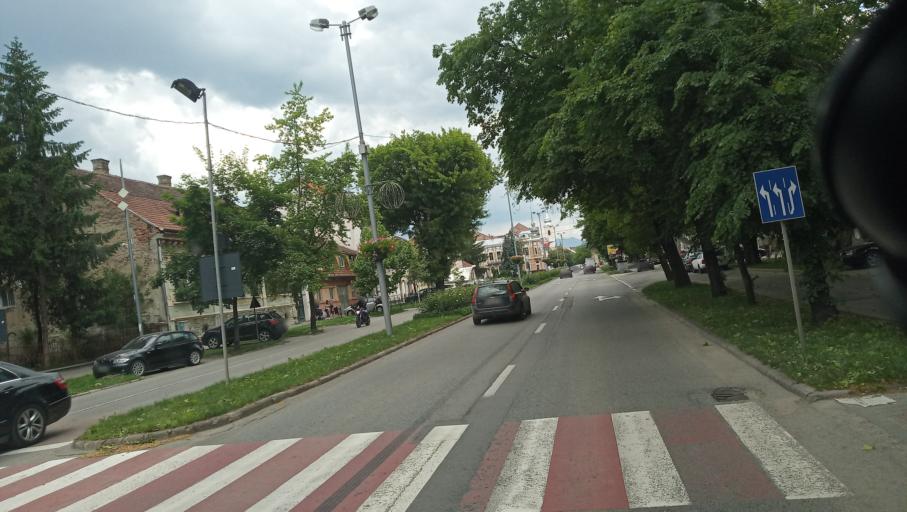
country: RO
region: Bistrita-Nasaud
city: Bistrita
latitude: 47.1290
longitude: 24.4890
